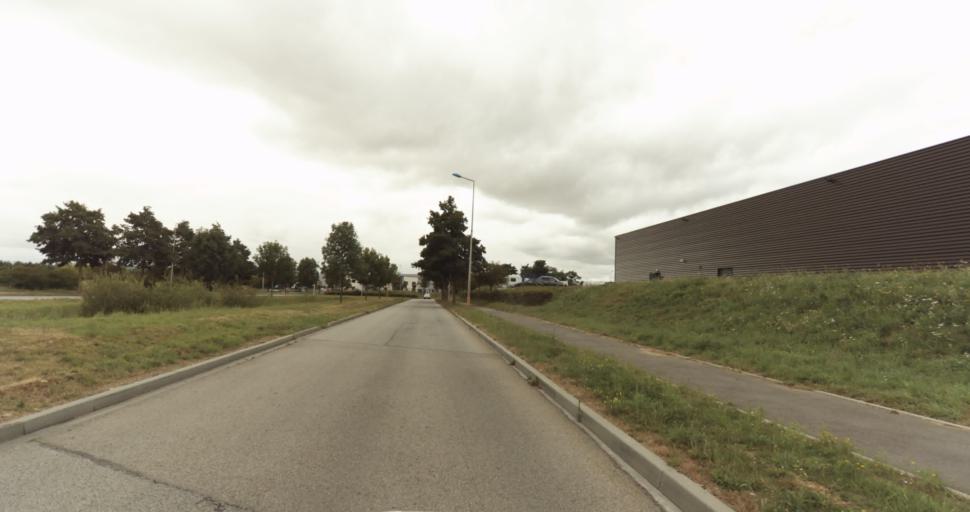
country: FR
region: Haute-Normandie
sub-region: Departement de l'Eure
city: Evreux
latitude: 49.0116
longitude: 1.1787
